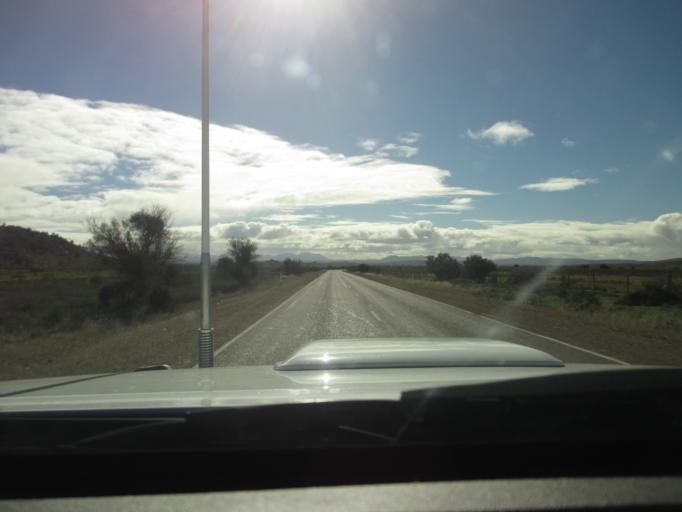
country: AU
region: South Australia
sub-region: Flinders Ranges
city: Quorn
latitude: -31.9176
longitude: 138.4270
